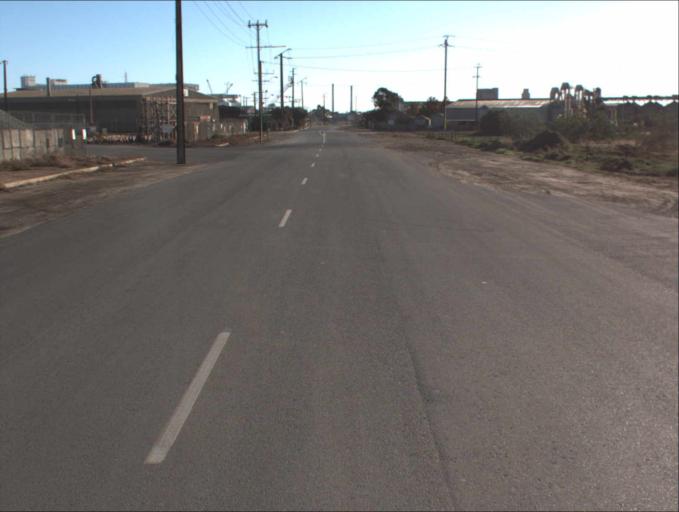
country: AU
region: South Australia
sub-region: Port Adelaide Enfield
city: Birkenhead
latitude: -34.8366
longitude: 138.5125
